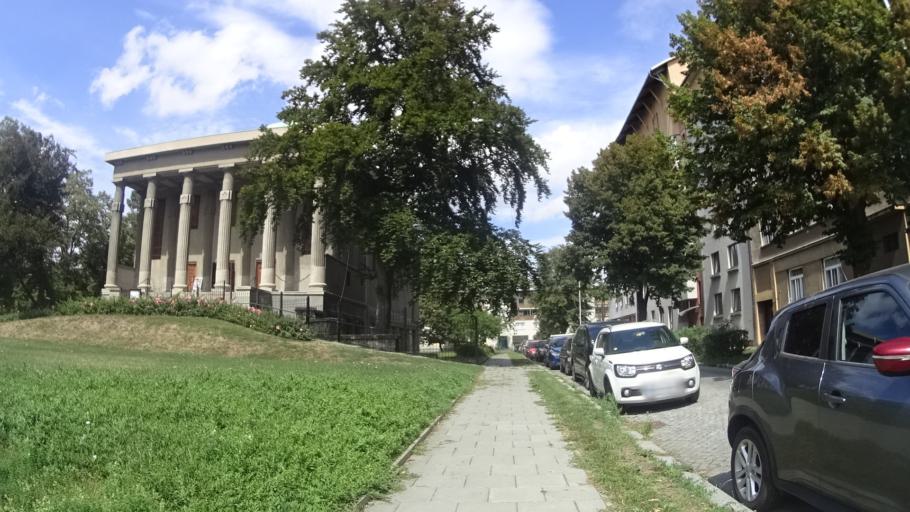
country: CZ
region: Olomoucky
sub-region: Okres Olomouc
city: Olomouc
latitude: 49.5974
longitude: 17.2475
